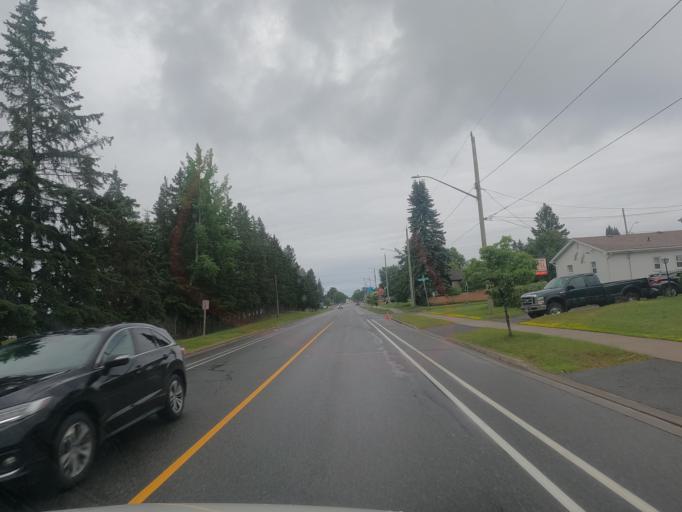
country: CA
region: Ontario
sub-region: Thunder Bay District
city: Thunder Bay
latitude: 48.4711
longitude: -89.1822
